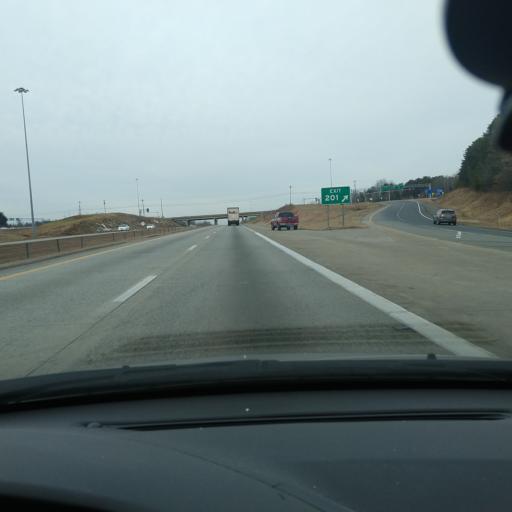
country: US
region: North Carolina
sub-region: Forsyth County
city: Kernersville
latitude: 36.0752
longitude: -80.1057
